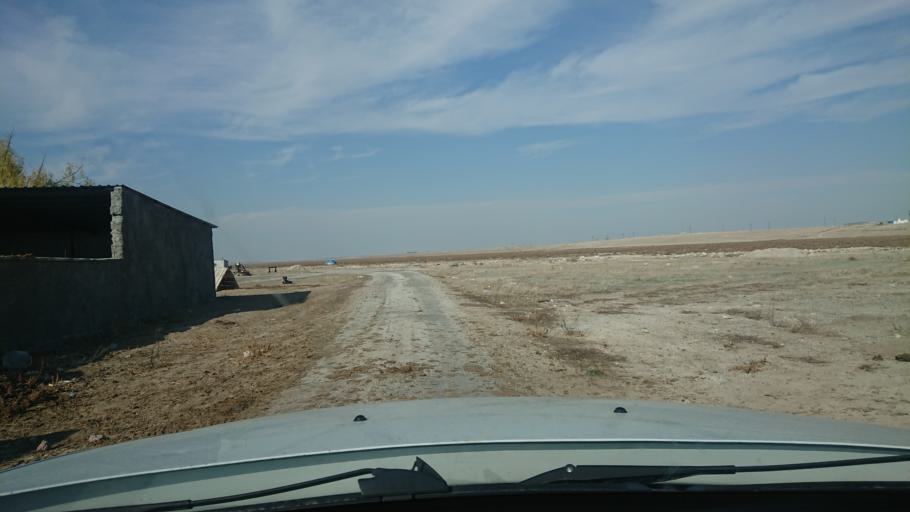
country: TR
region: Aksaray
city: Sultanhani
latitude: 38.2597
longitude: 33.4745
